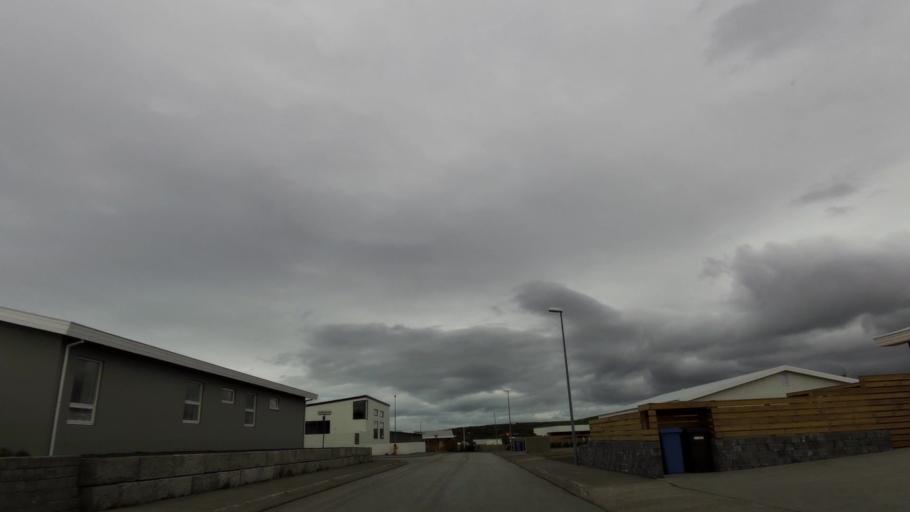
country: IS
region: Capital Region
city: Hafnarfjoerdur
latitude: 64.0426
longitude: -21.9666
